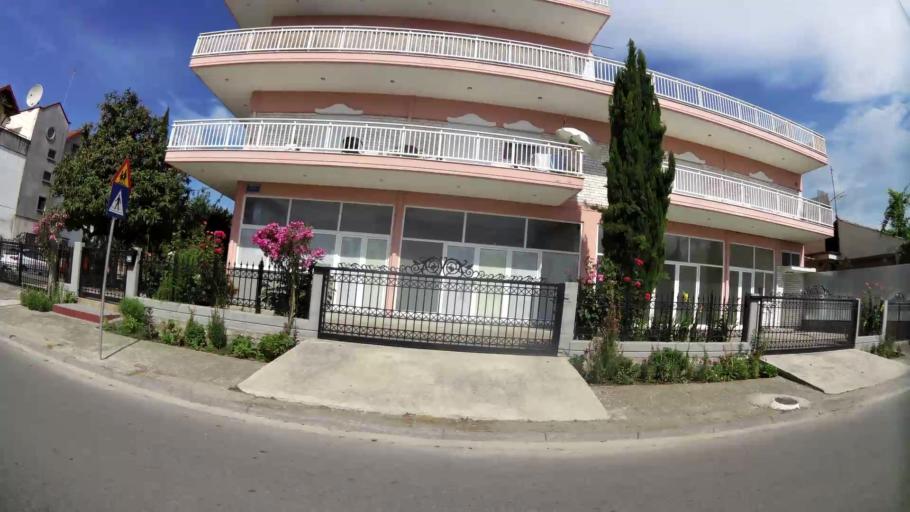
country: GR
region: Central Macedonia
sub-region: Nomos Pierias
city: Katerini
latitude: 40.2822
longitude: 22.5079
